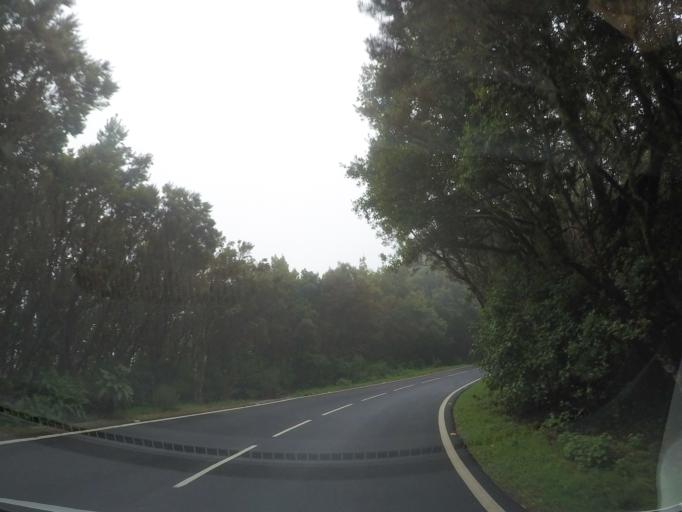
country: ES
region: Canary Islands
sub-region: Provincia de Santa Cruz de Tenerife
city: Vallehermosa
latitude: 28.1415
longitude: -17.2841
